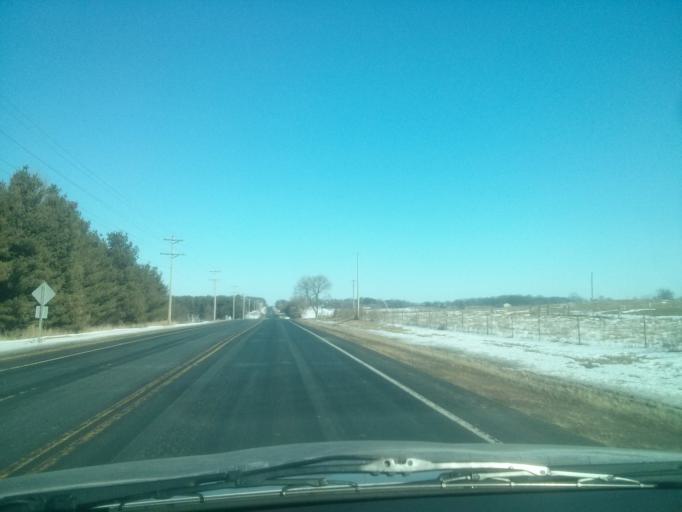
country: US
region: Minnesota
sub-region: Washington County
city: Bayport
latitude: 45.0706
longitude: -92.7361
